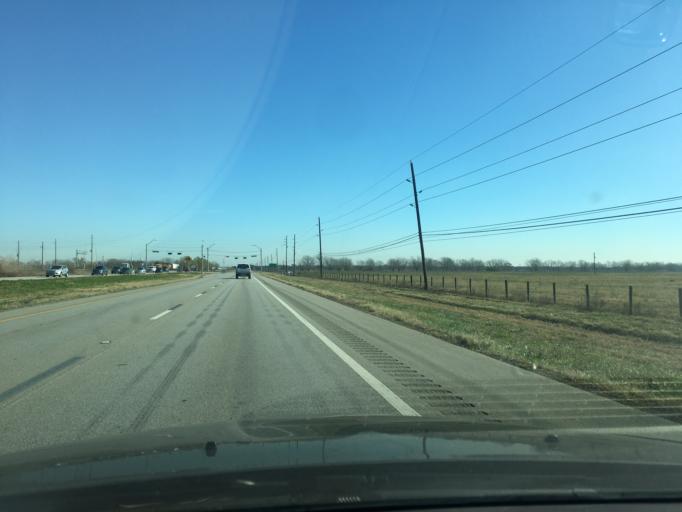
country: US
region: Texas
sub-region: Fort Bend County
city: Pecan Grove
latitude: 29.5983
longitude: -95.7161
